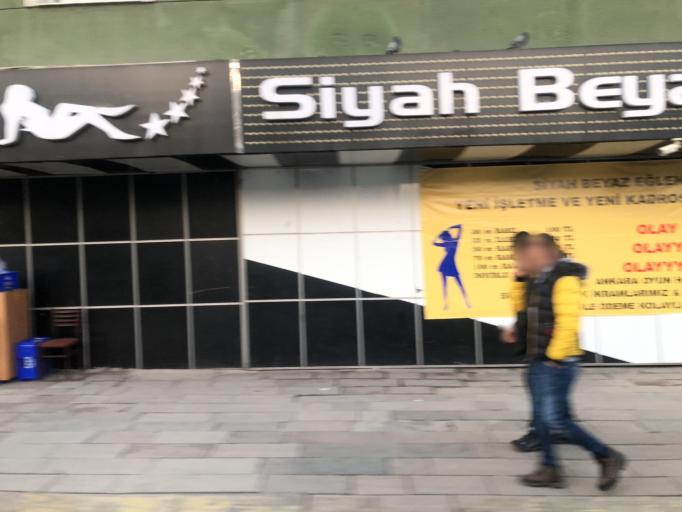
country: TR
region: Ankara
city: Ankara
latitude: 39.9440
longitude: 32.8545
